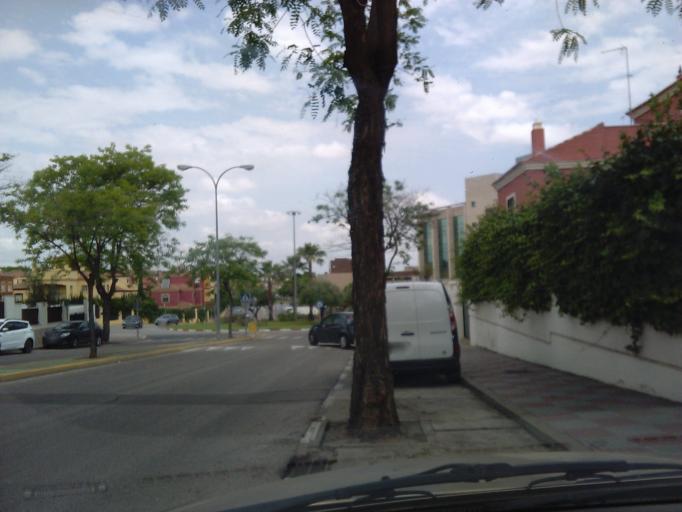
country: ES
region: Andalusia
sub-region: Provincia de Sevilla
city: Tomares
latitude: 37.3670
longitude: -6.0417
